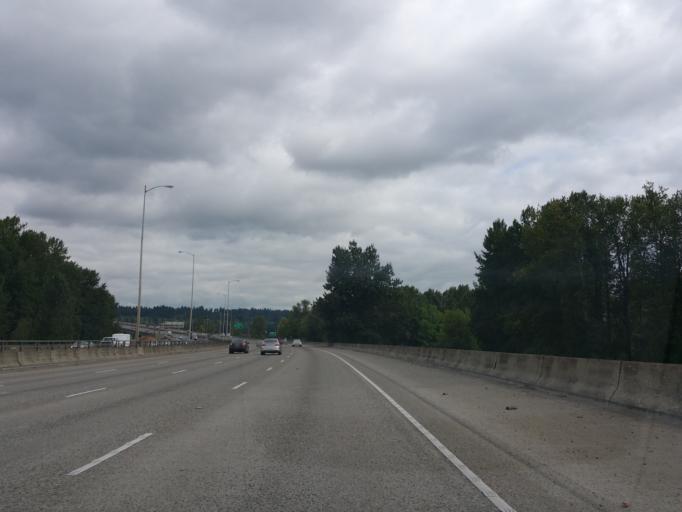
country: US
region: Washington
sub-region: Clark County
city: Mill Plain
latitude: 45.5792
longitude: -122.5437
